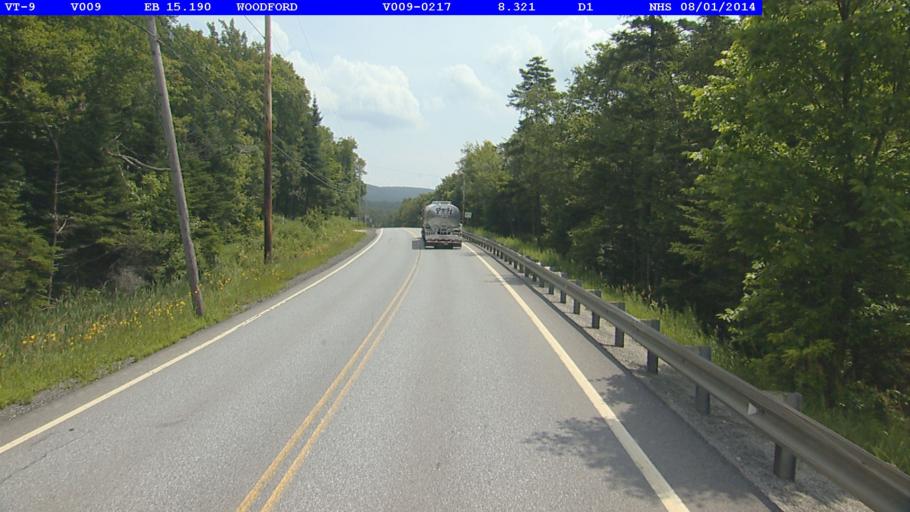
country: US
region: Vermont
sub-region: Bennington County
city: Bennington
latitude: 42.8917
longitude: -73.0344
